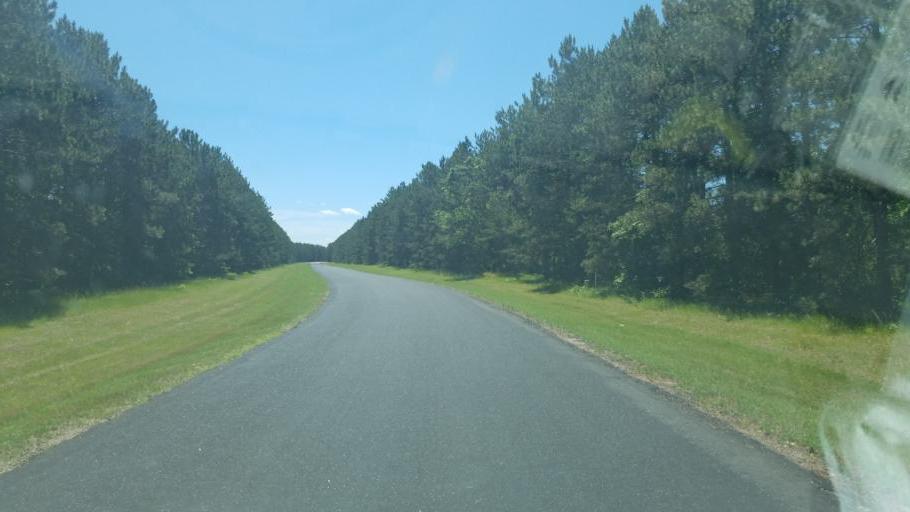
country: US
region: Wisconsin
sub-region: Juneau County
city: New Lisbon
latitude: 44.0518
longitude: -90.0285
